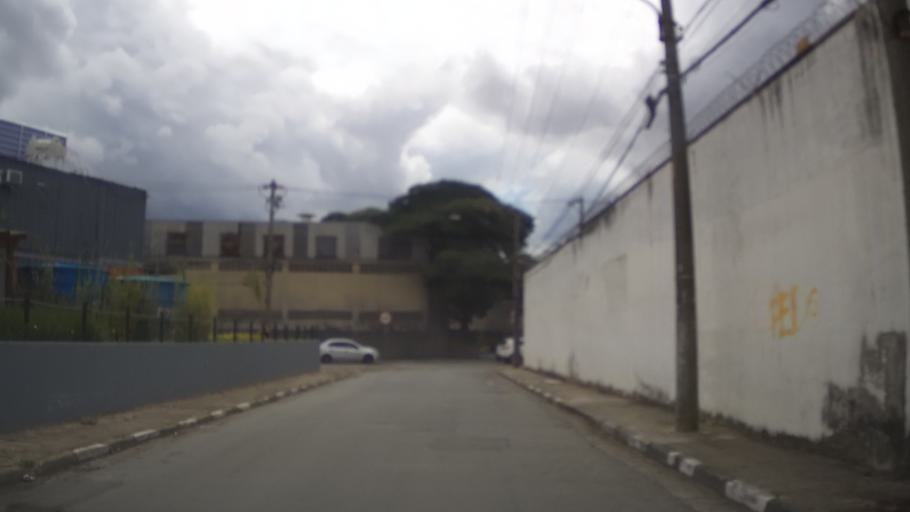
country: BR
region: Sao Paulo
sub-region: Guarulhos
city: Guarulhos
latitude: -23.4914
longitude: -46.5524
